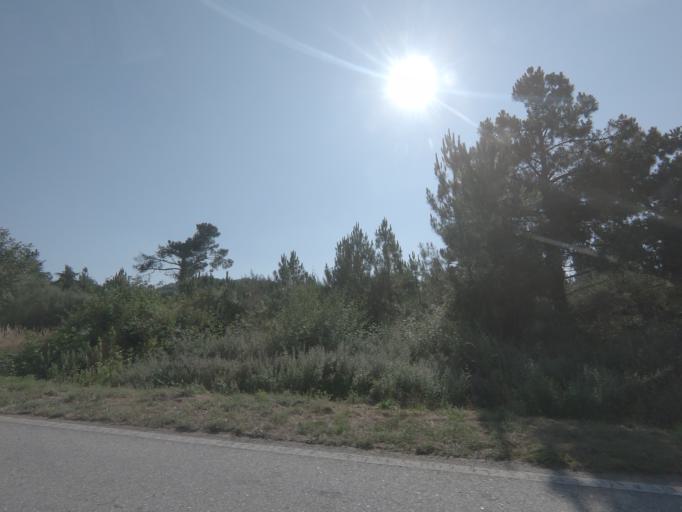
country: PT
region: Viseu
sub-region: Moimenta da Beira
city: Moimenta da Beira
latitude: 41.0348
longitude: -7.5682
